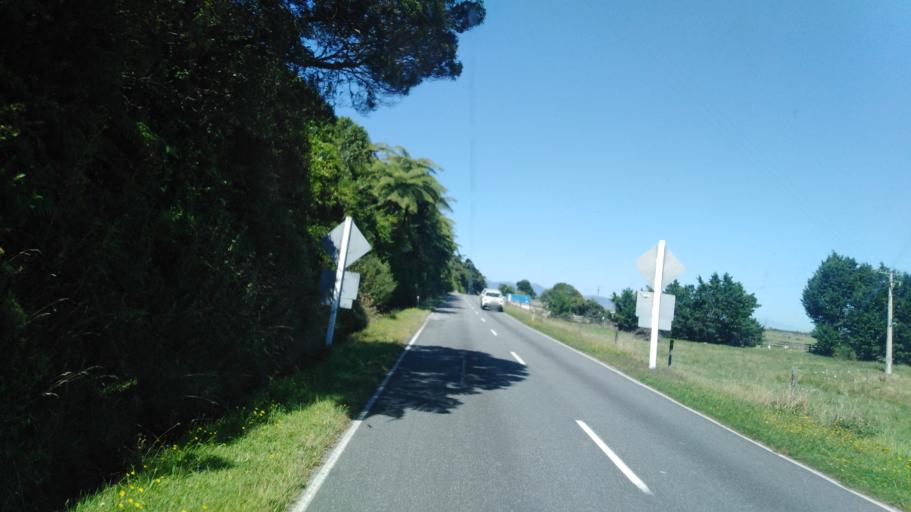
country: NZ
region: West Coast
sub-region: Buller District
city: Westport
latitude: -41.2579
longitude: 172.1130
